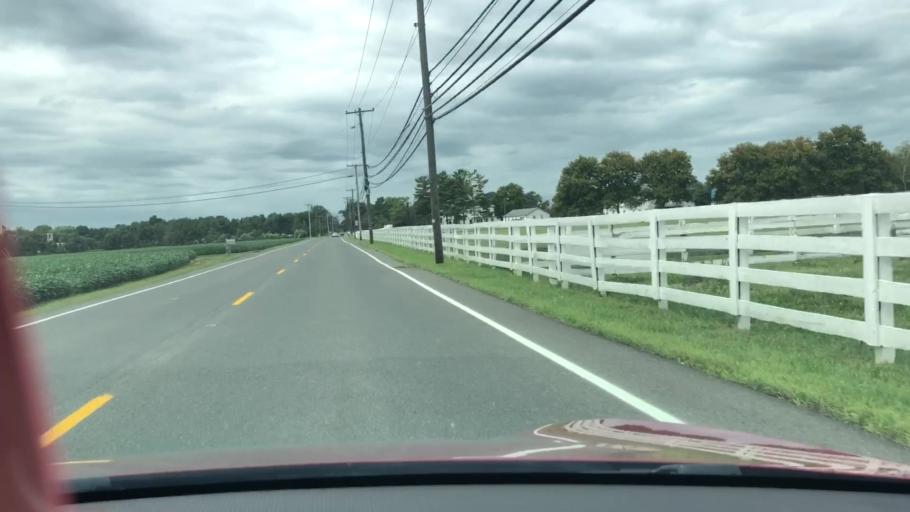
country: US
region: New Jersey
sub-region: Monmouth County
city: Shrewsbury
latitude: 40.1691
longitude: -74.5264
